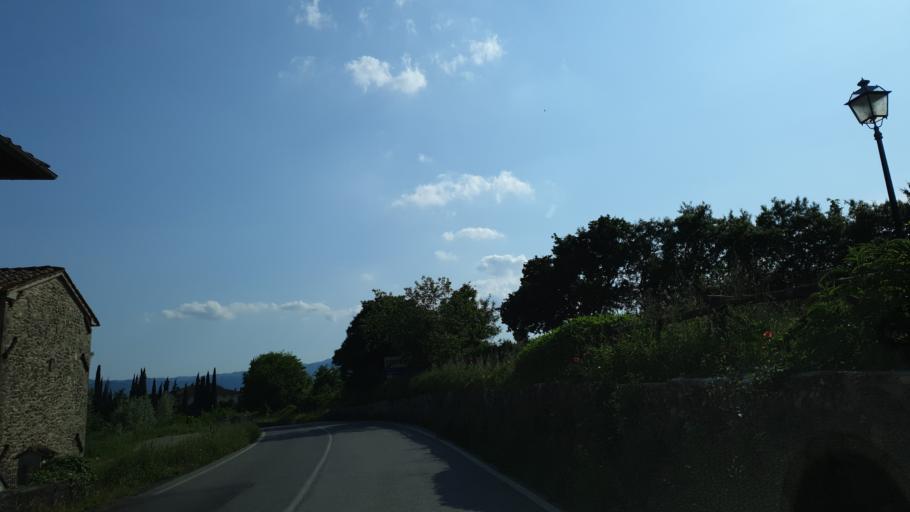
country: IT
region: Tuscany
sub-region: Province of Arezzo
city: Soci
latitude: 43.7457
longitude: 11.8181
